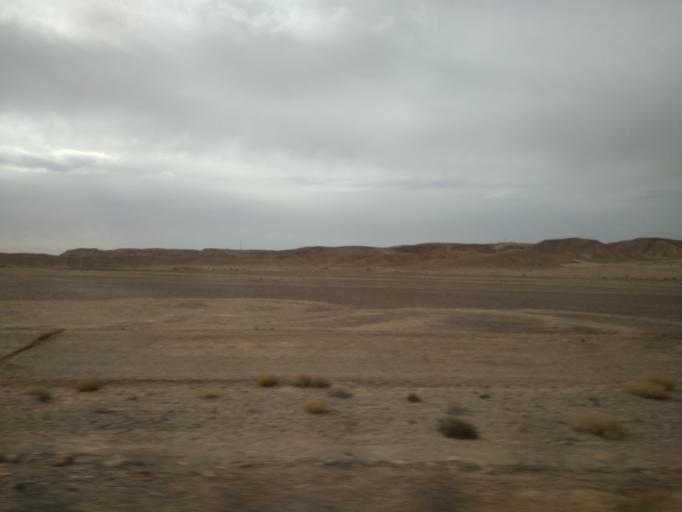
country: IL
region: Southern District
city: Eilat
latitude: 29.9019
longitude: 34.8616
